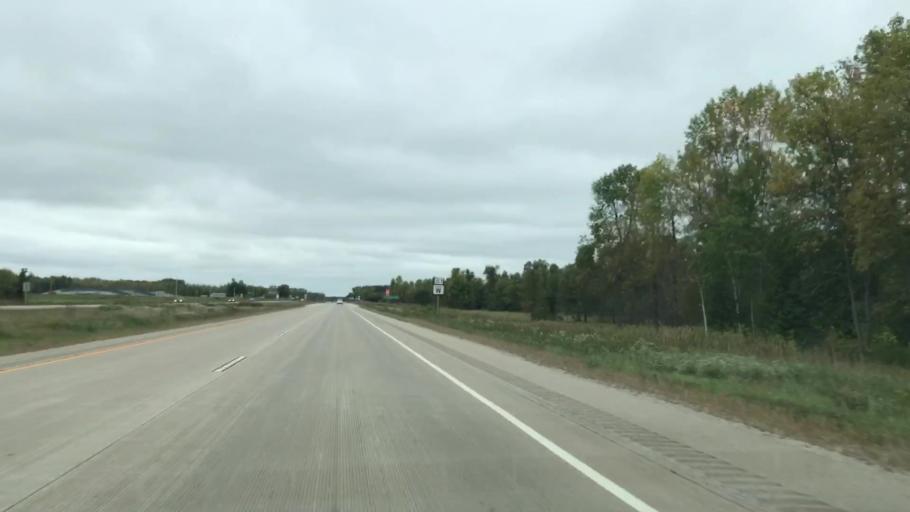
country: US
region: Wisconsin
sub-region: Oconto County
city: Oconto
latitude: 44.9936
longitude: -87.8563
